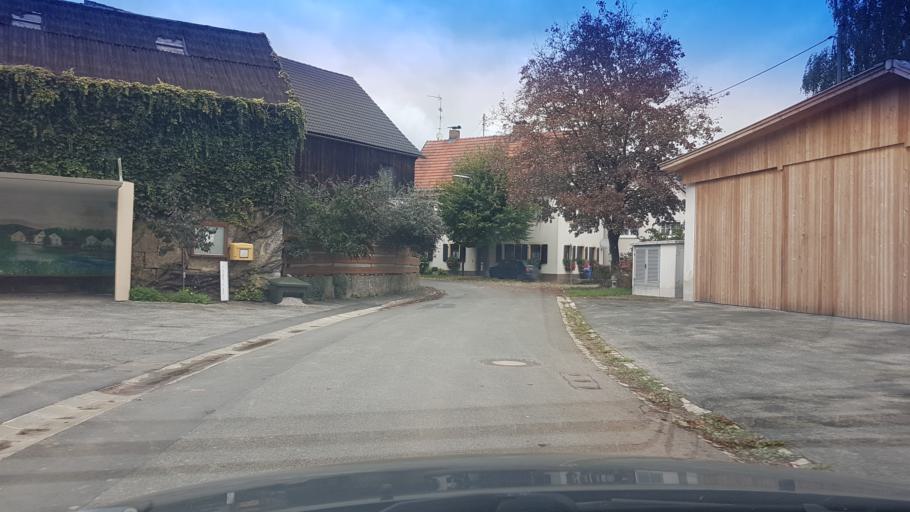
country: DE
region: Bavaria
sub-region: Upper Franconia
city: Wonsees
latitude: 50.0103
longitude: 11.2589
